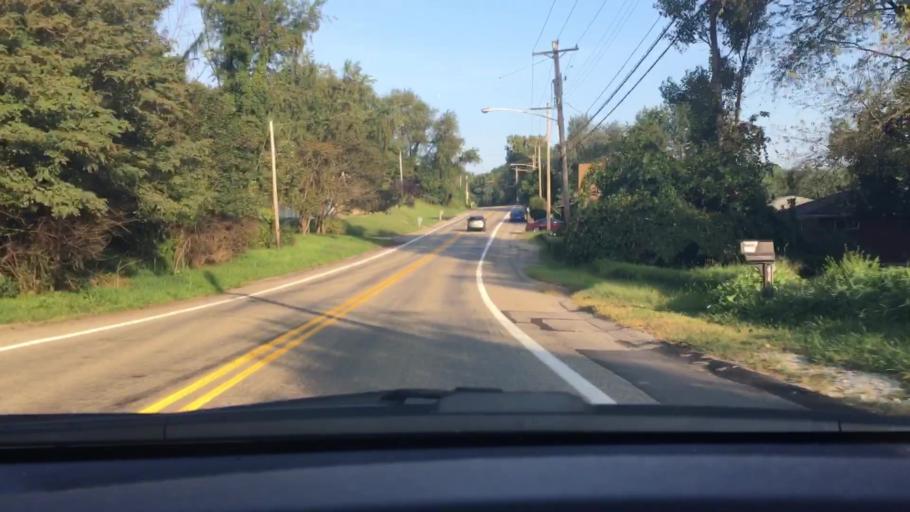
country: US
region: Pennsylvania
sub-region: Allegheny County
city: Liberty
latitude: 40.3209
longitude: -79.8676
